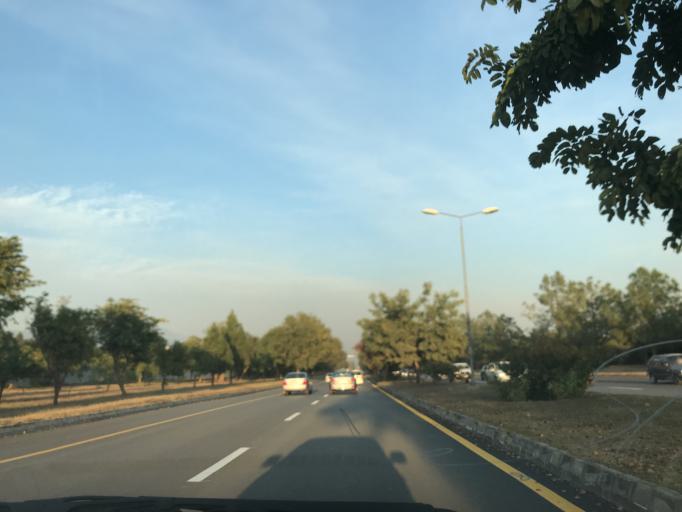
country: PK
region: Islamabad
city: Islamabad
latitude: 33.7108
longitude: 73.0222
